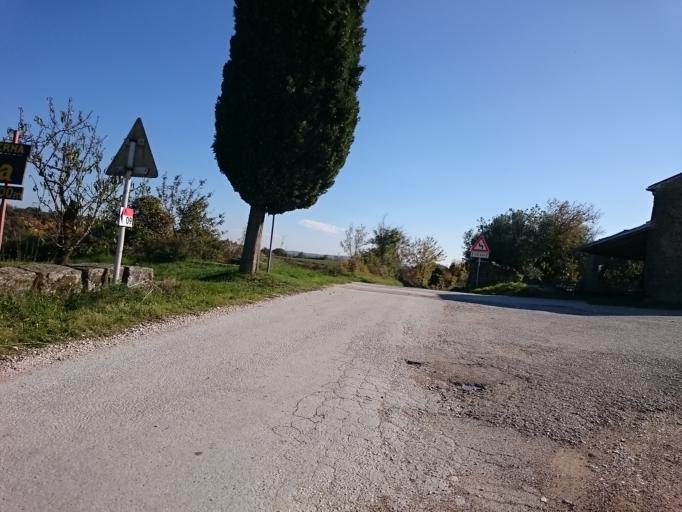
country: HR
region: Istarska
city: Buje
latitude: 45.4373
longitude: 13.7178
